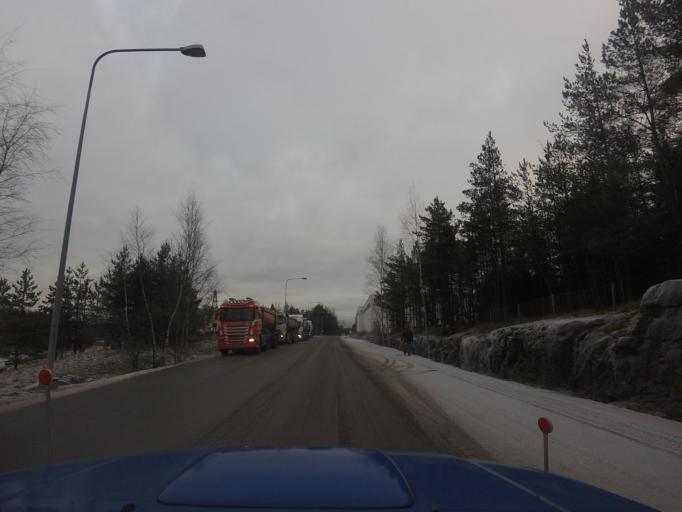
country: FI
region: Uusimaa
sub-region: Helsinki
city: Espoo
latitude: 60.2069
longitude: 24.6273
